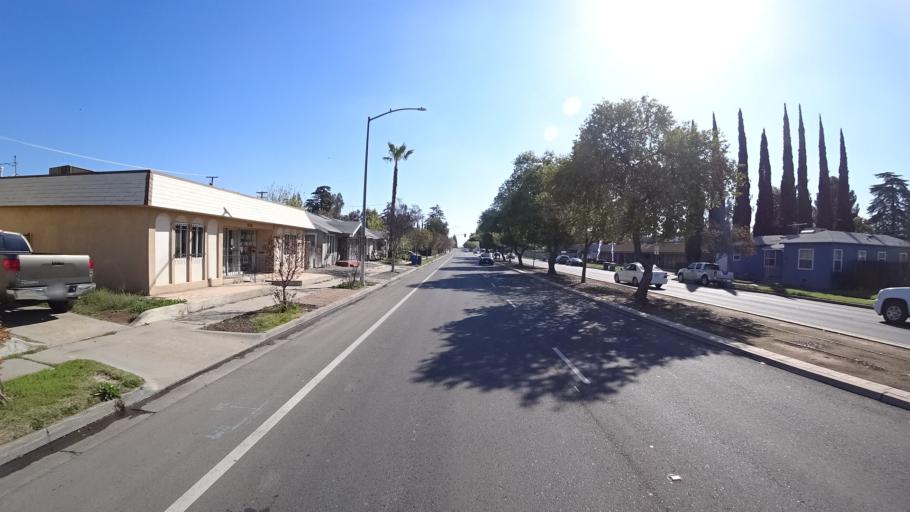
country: US
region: California
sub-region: Fresno County
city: Fresno
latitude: 36.7795
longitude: -119.8057
